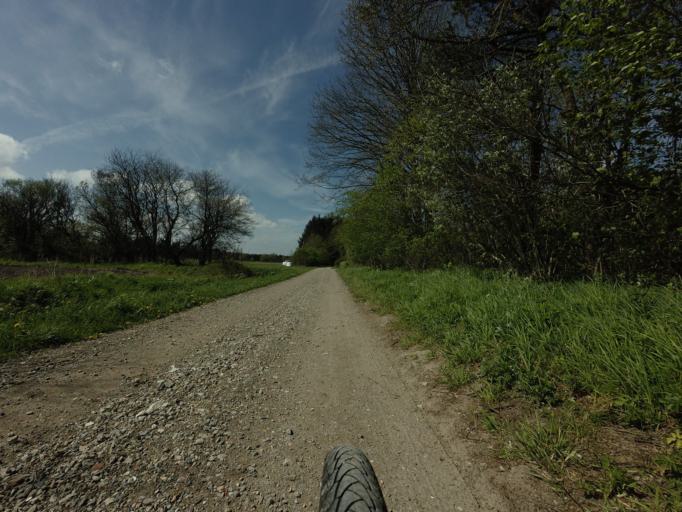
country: DK
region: North Denmark
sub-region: Jammerbugt Kommune
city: Brovst
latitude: 57.1555
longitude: 9.5639
